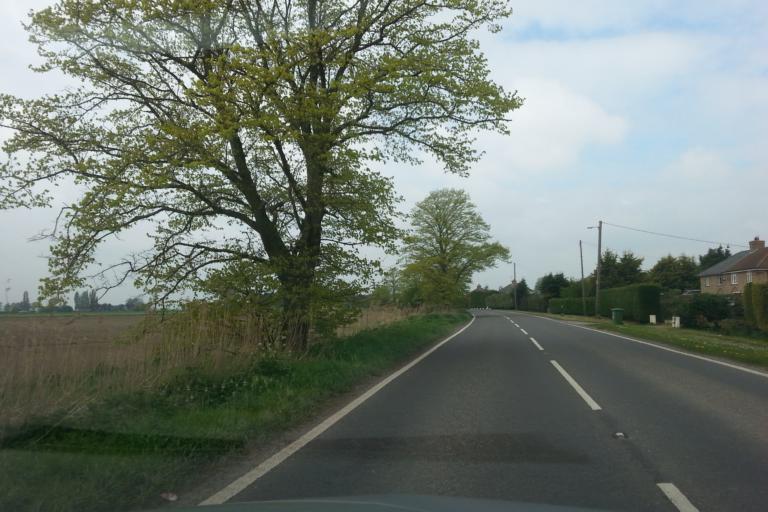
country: GB
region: England
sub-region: Norfolk
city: Outwell
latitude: 52.5715
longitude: 0.2279
